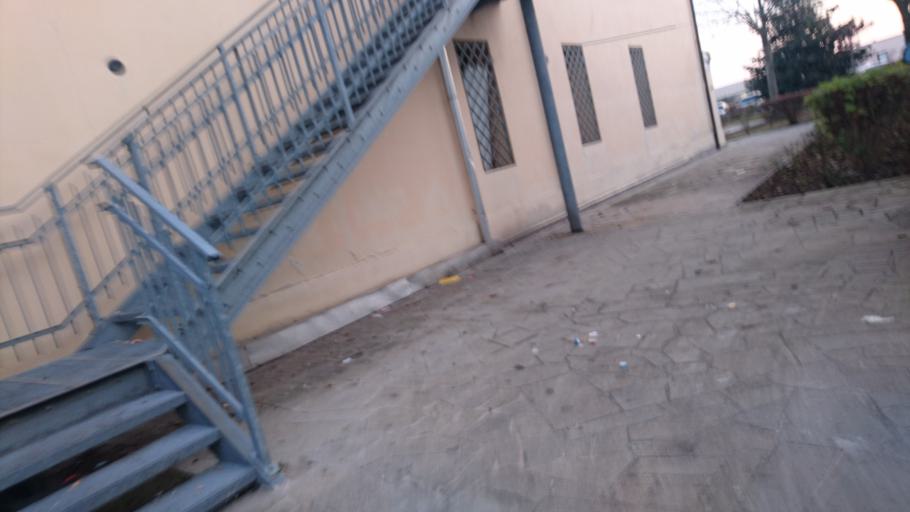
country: IT
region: Veneto
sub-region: Provincia di Padova
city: Casalserugo
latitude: 45.3158
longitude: 11.9129
